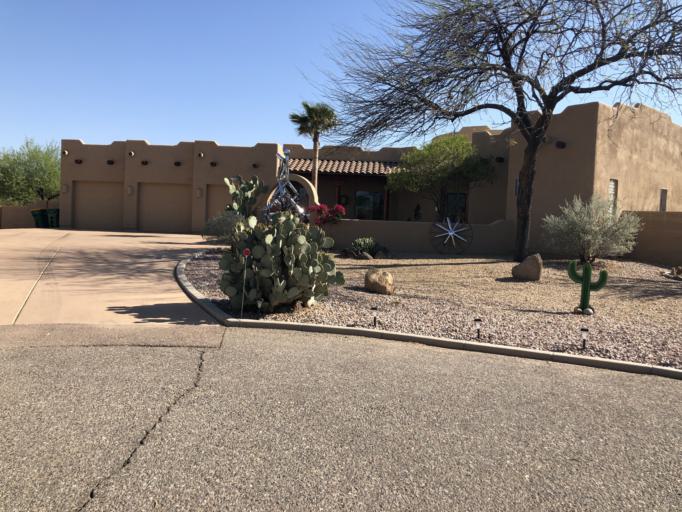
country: US
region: Arizona
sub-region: Maricopa County
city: Anthem
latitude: 33.8378
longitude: -112.0725
